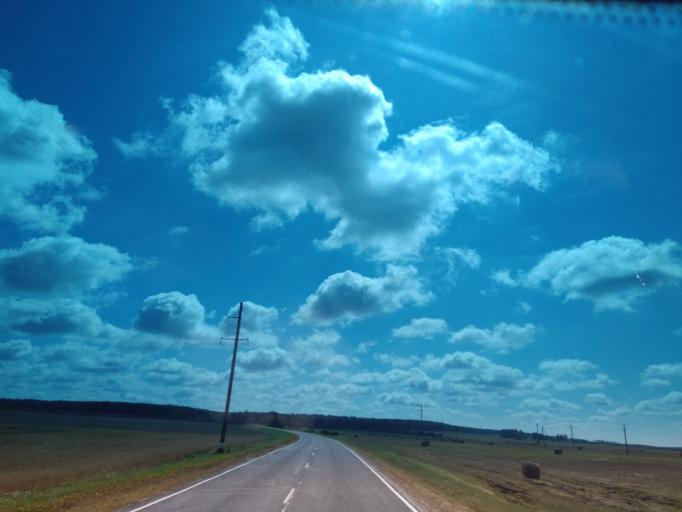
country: BY
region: Minsk
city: Uzda
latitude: 53.3957
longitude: 27.2324
